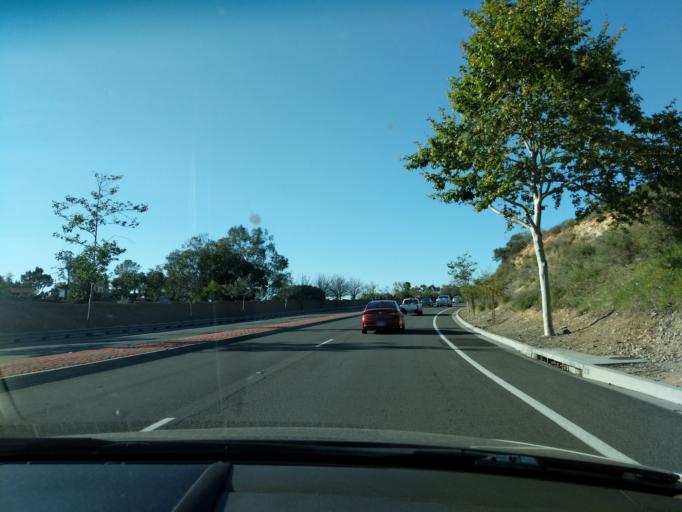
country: US
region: California
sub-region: San Diego County
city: Lake San Marcos
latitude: 33.1137
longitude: -117.2266
